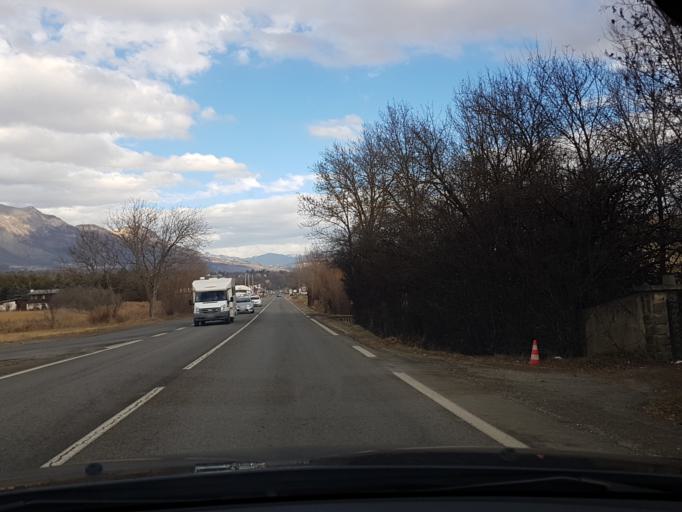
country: FR
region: Provence-Alpes-Cote d'Azur
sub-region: Departement des Hautes-Alpes
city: Tallard
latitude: 44.5041
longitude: 6.0440
